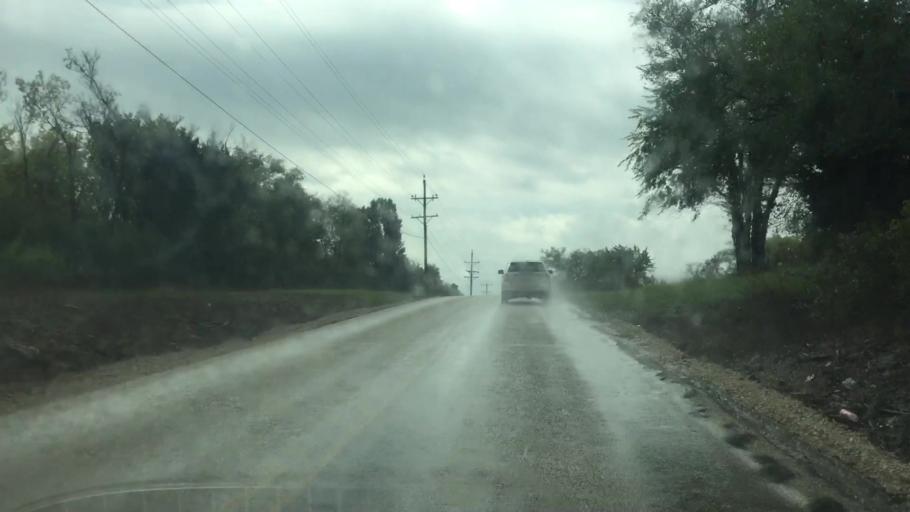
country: US
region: Kansas
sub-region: Allen County
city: Humboldt
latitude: 37.8620
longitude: -95.4369
